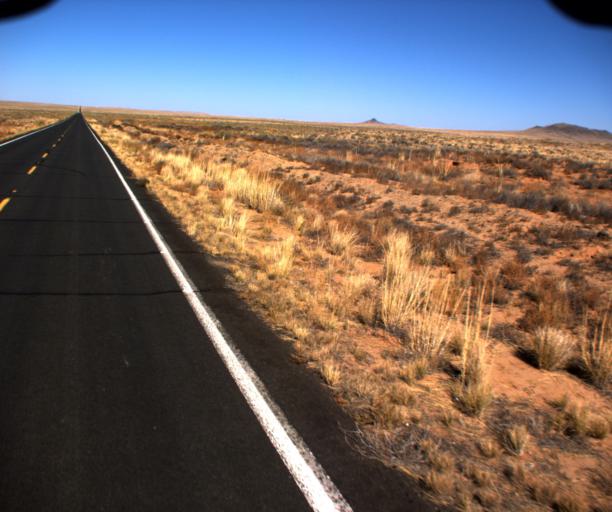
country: US
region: Arizona
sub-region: Navajo County
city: Dilkon
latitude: 35.5670
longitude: -110.4588
